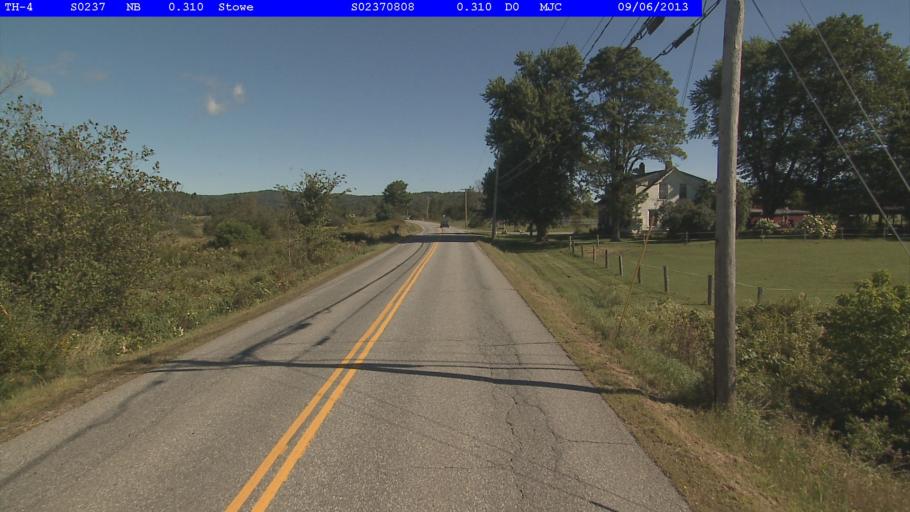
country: US
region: Vermont
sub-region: Lamoille County
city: Morristown
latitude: 44.4859
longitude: -72.6623
